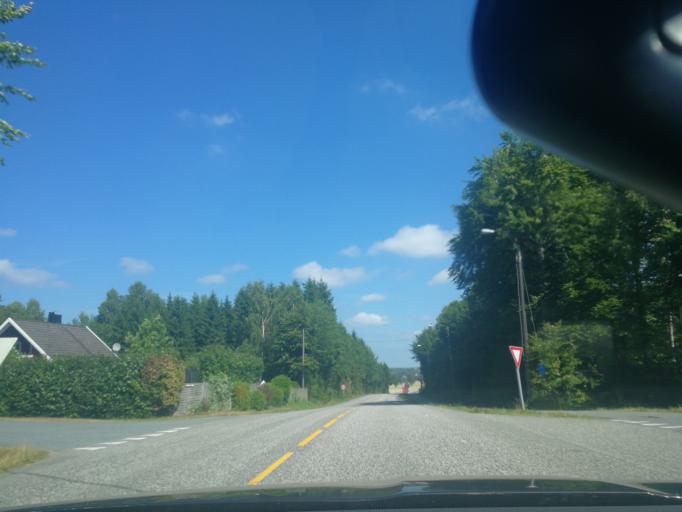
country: NO
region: Vestfold
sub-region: Sandefjord
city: Sandefjord
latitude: 59.1820
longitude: 10.2157
